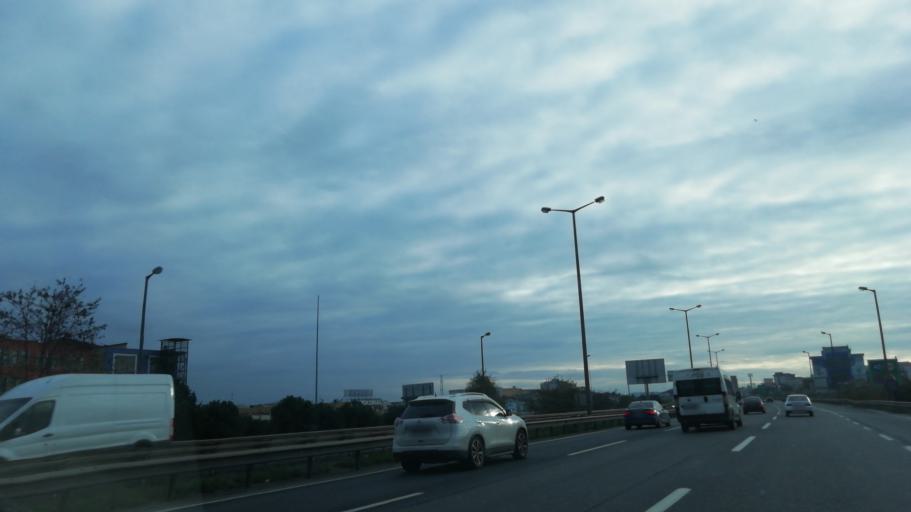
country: TR
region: Istanbul
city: Samandira
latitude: 40.9914
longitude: 29.1744
